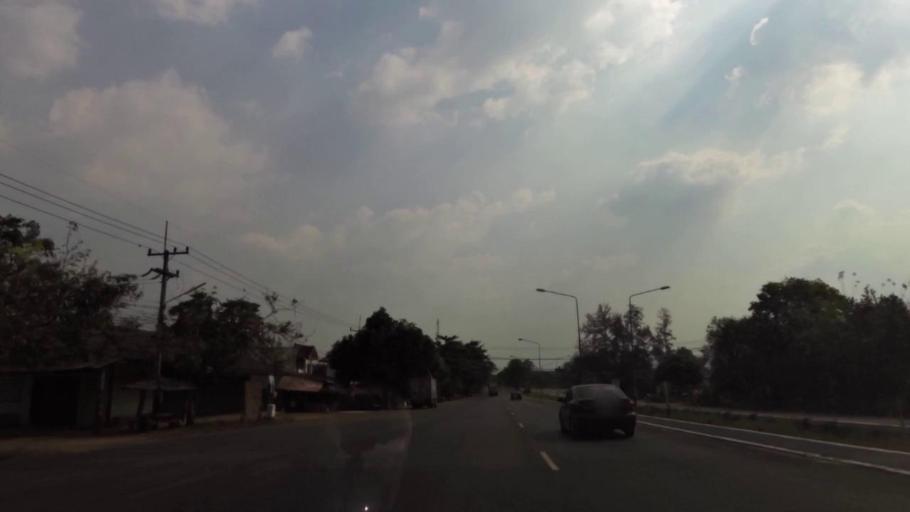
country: TH
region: Rayong
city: Wang Chan
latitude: 13.0338
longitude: 101.4357
